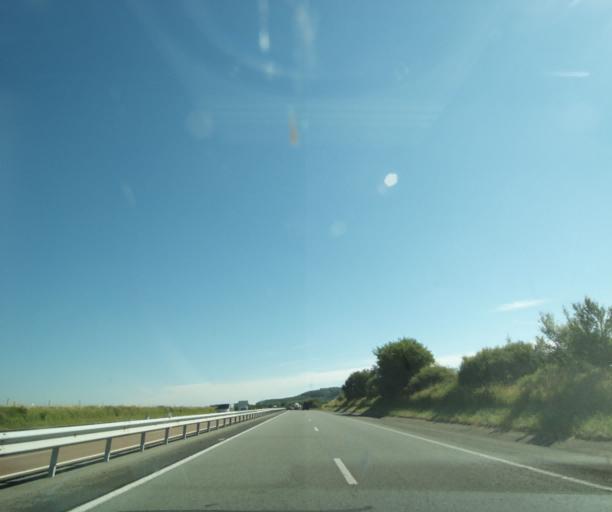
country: FR
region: Champagne-Ardenne
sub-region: Departement de la Haute-Marne
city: Avrecourt
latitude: 48.0467
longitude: 5.5723
